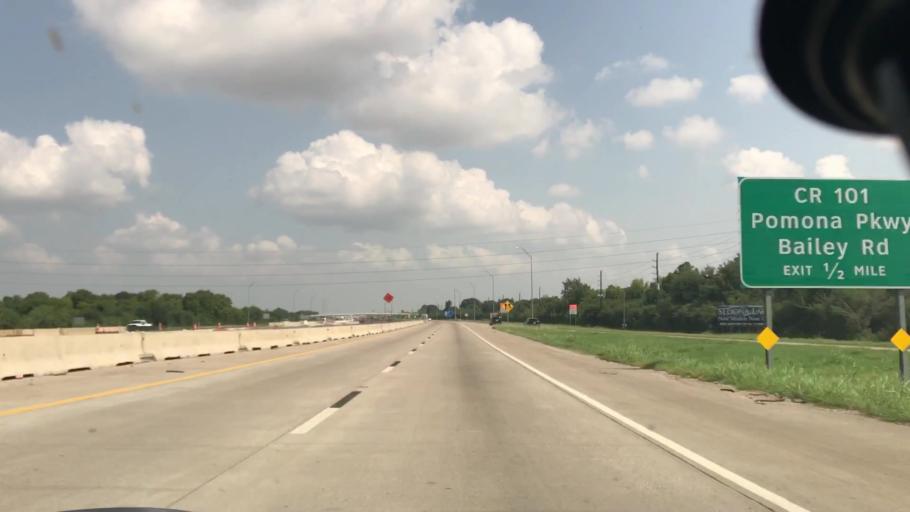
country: US
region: Texas
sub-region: Brazoria County
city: Iowa Colony
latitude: 29.5153
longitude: -95.3868
